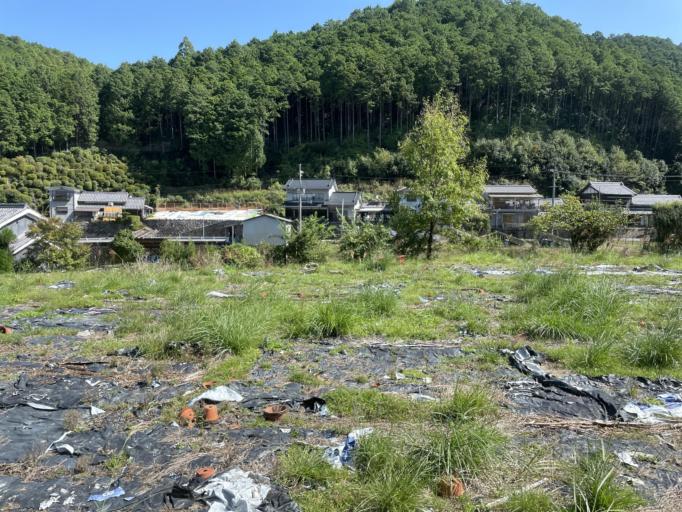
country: JP
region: Nara
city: Yoshino-cho
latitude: 34.3830
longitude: 135.8519
